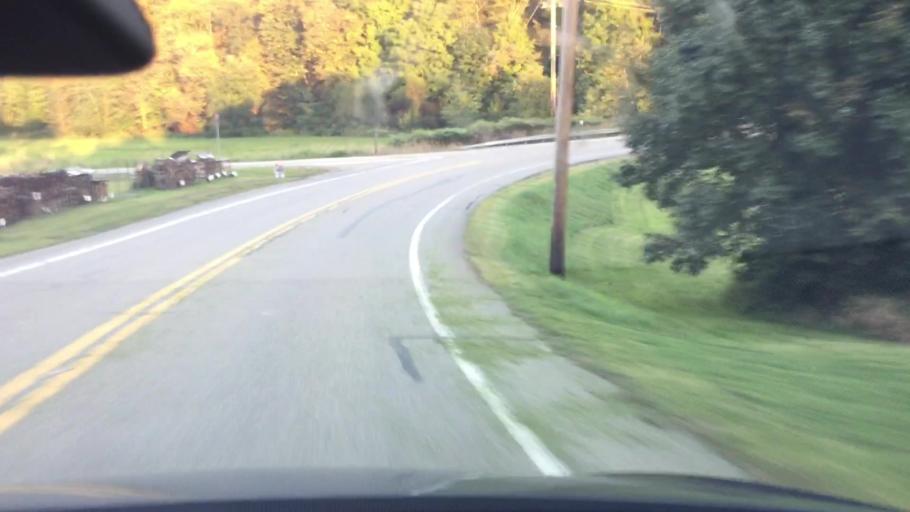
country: US
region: Pennsylvania
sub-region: Allegheny County
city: Curtisville
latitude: 40.6118
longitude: -79.8967
